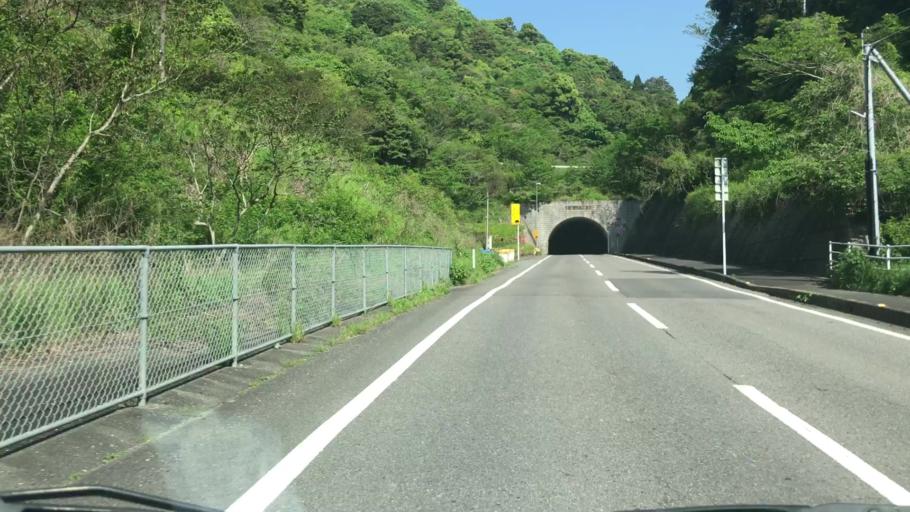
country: JP
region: Saga Prefecture
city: Takeocho-takeo
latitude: 33.2130
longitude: 130.0076
